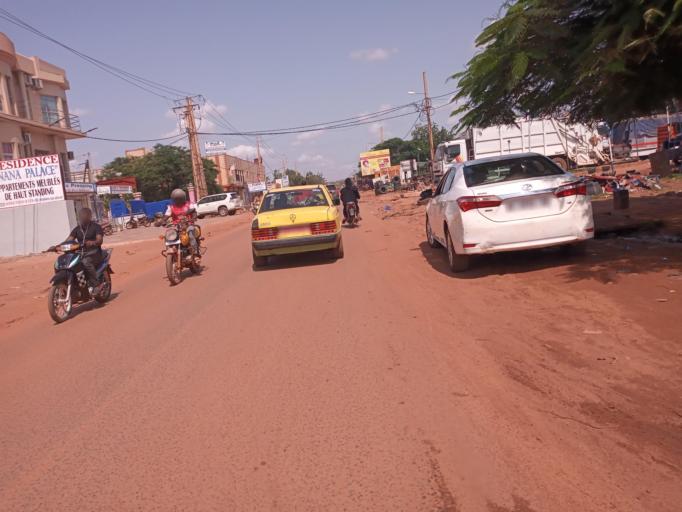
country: ML
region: Bamako
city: Bamako
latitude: 12.5969
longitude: -8.0219
